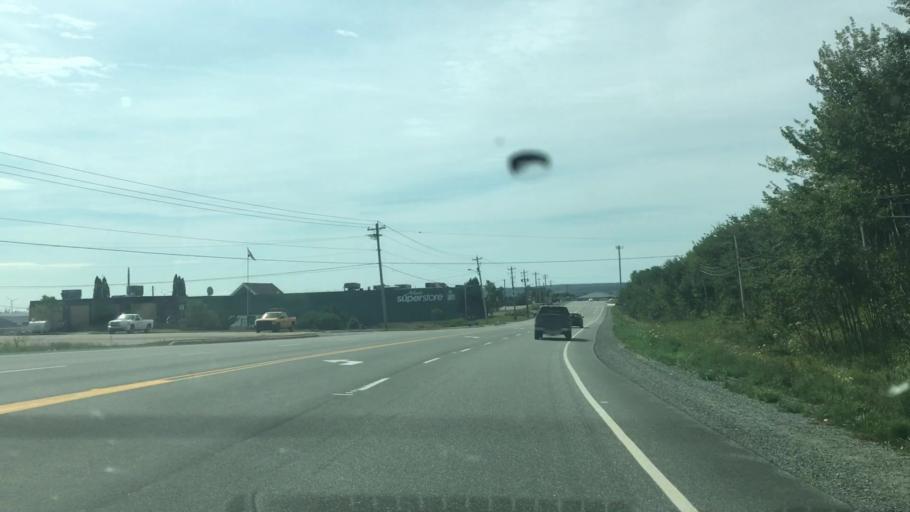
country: CA
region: Nova Scotia
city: Port Hawkesbury
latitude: 45.6211
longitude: -61.3337
